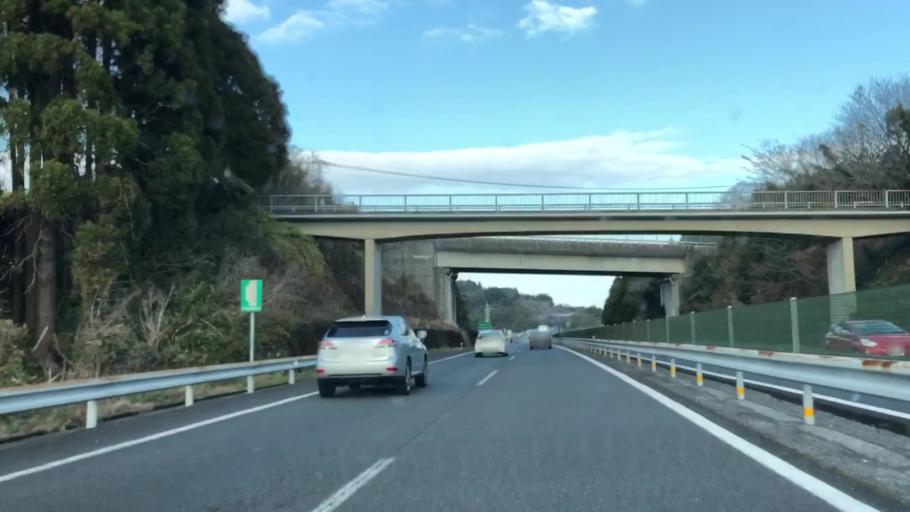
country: JP
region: Miyazaki
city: Miyazaki-shi
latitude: 31.8577
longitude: 131.3763
